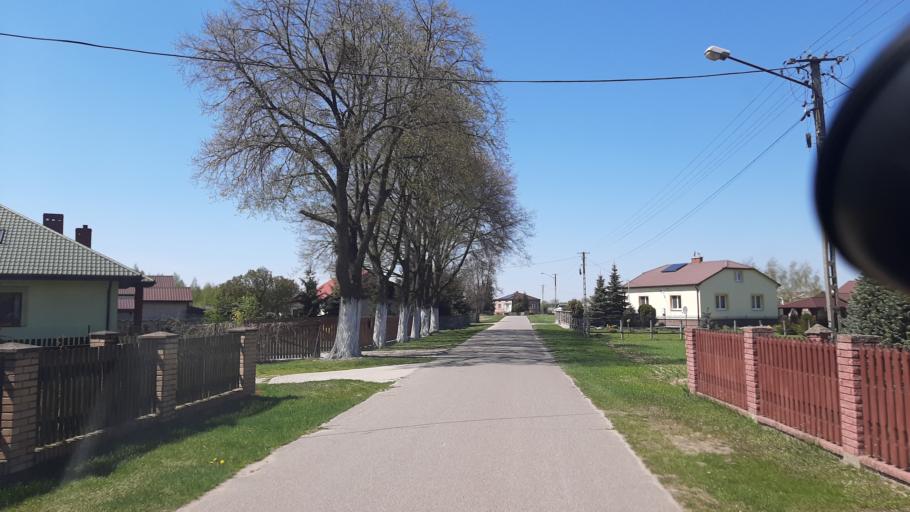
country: PL
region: Lublin Voivodeship
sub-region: Powiat lubelski
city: Garbow
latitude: 51.4019
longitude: 22.3276
